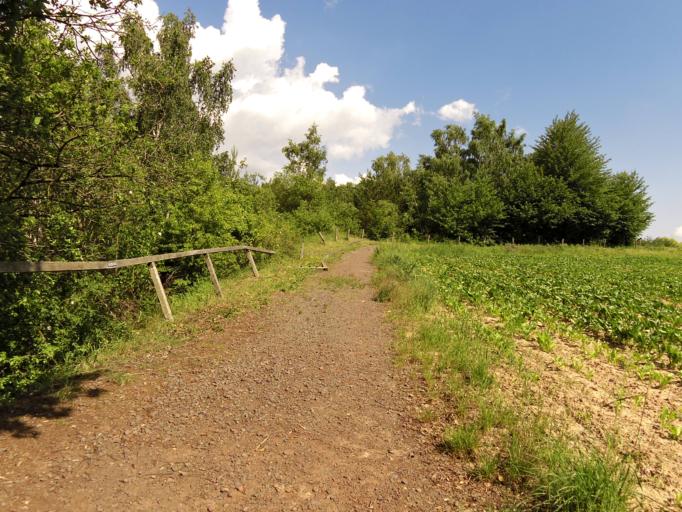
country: DE
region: Rheinland-Pfalz
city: Eisenberg
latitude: 49.5488
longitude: 8.0759
